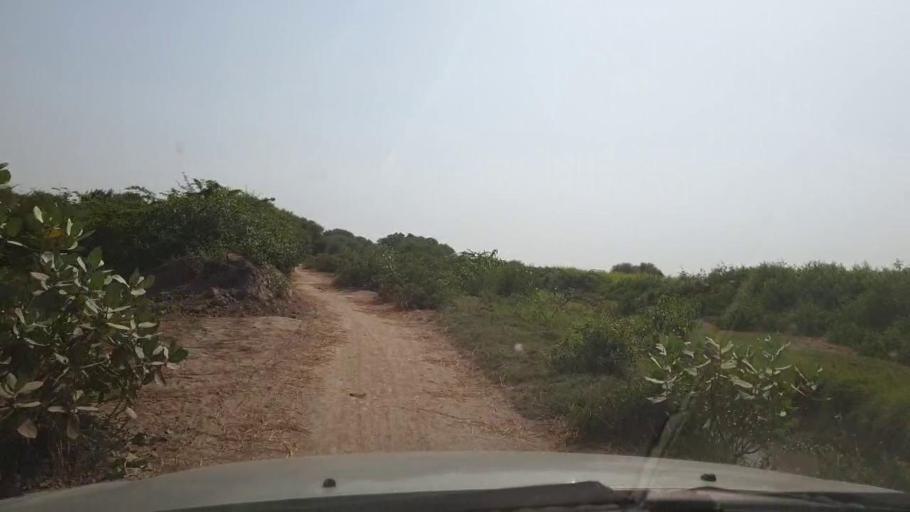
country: PK
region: Sindh
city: Bulri
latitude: 24.8700
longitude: 68.3108
